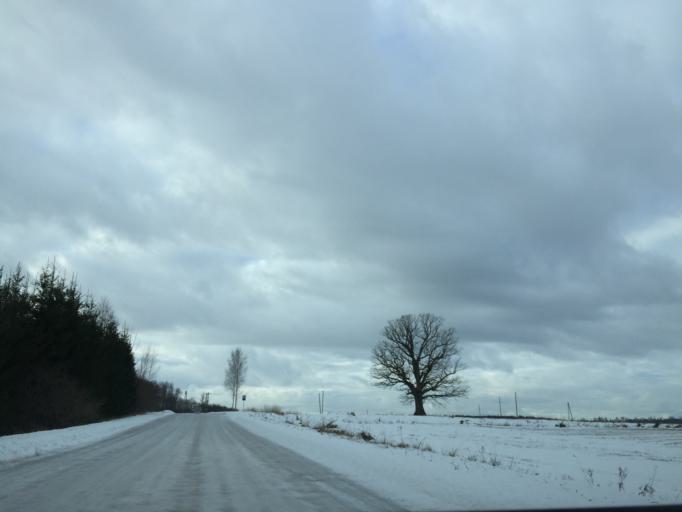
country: LV
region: Lielvarde
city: Lielvarde
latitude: 56.6013
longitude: 24.7449
